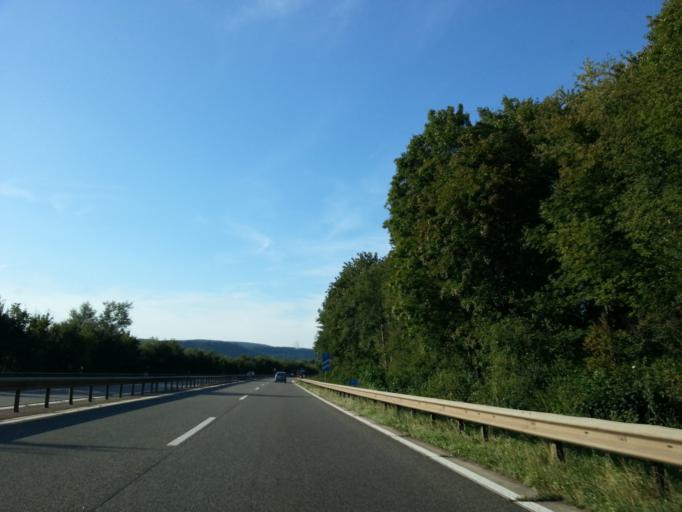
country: DE
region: Rheinland-Pfalz
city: Kenn
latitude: 49.7956
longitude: 6.7047
